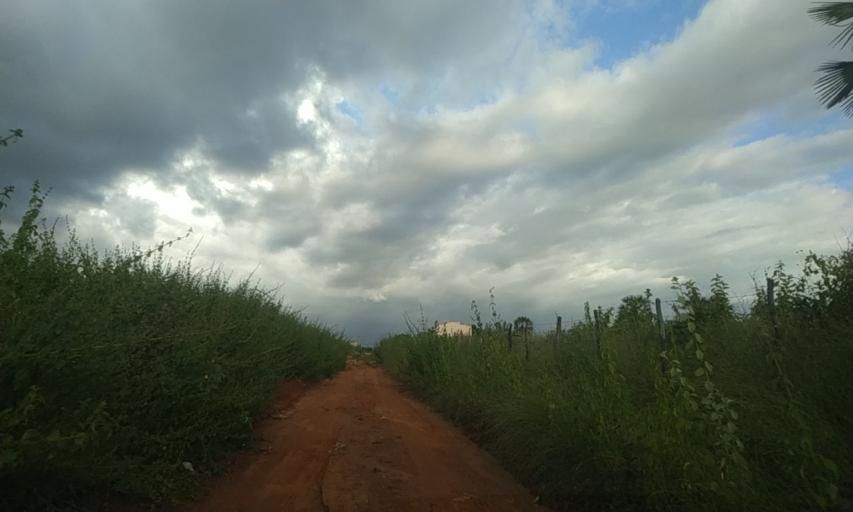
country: BR
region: Rio Grande do Norte
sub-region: Mossoro
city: Mossoro
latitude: -5.2205
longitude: -37.3443
